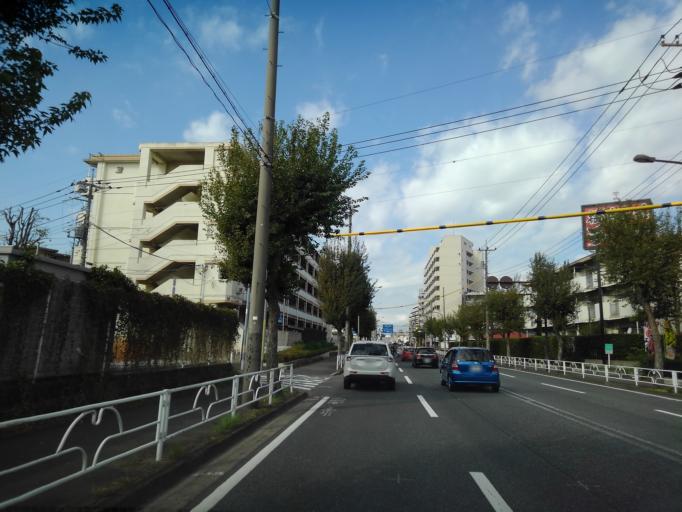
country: JP
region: Tokyo
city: Higashimurayama-shi
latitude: 35.7498
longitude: 139.4759
